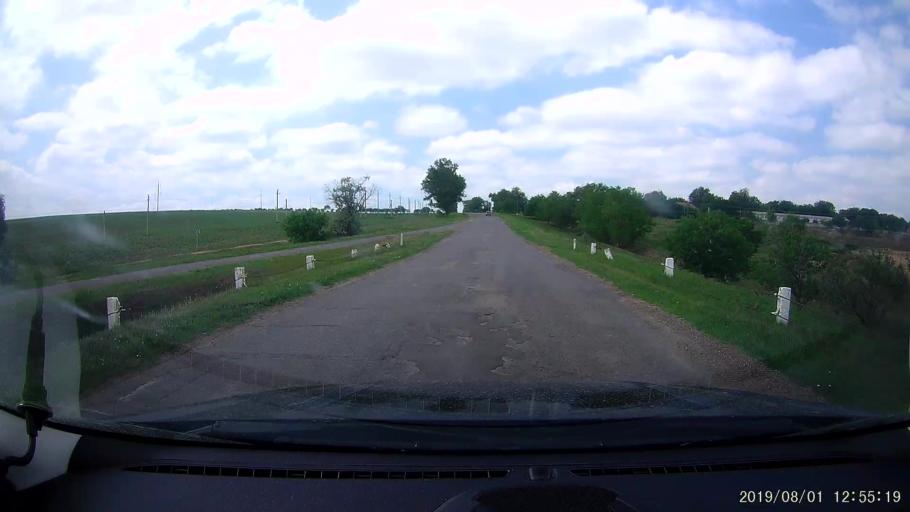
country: MD
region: Gagauzia
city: Vulcanesti
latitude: 45.6940
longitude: 28.4692
